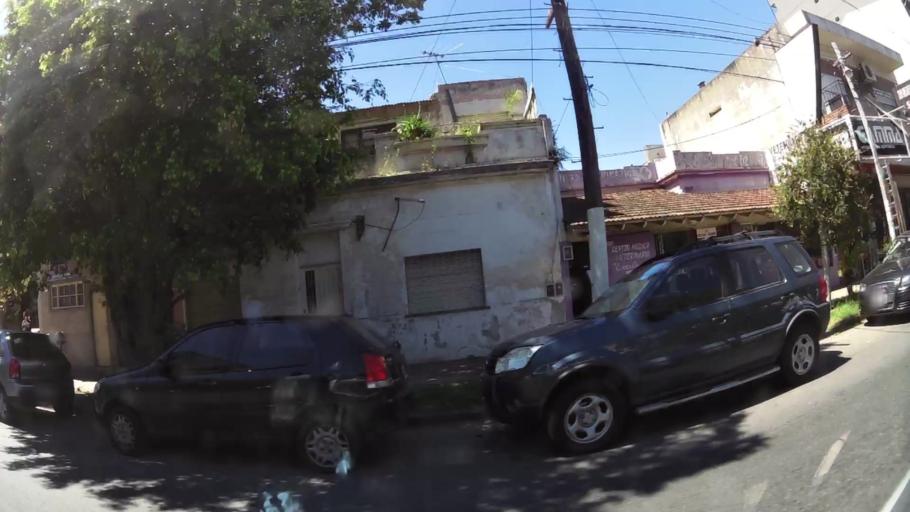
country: AR
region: Buenos Aires
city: Caseros
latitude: -34.6015
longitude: -58.5482
